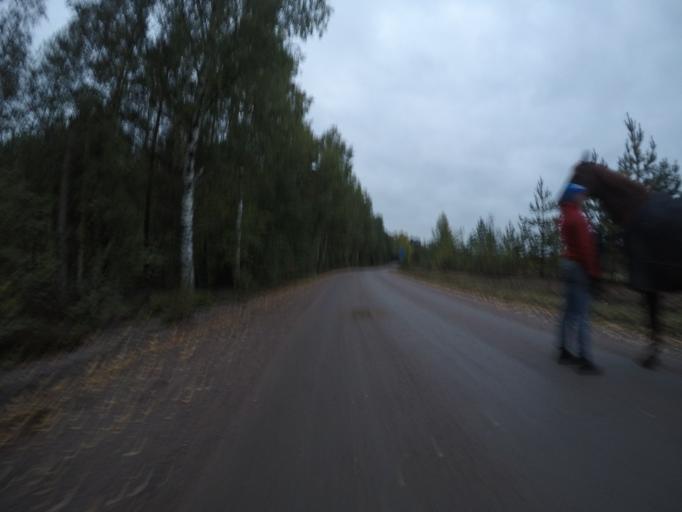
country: SE
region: Vaestmanland
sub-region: Kungsors Kommun
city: Kungsoer
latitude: 59.3894
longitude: 16.1171
